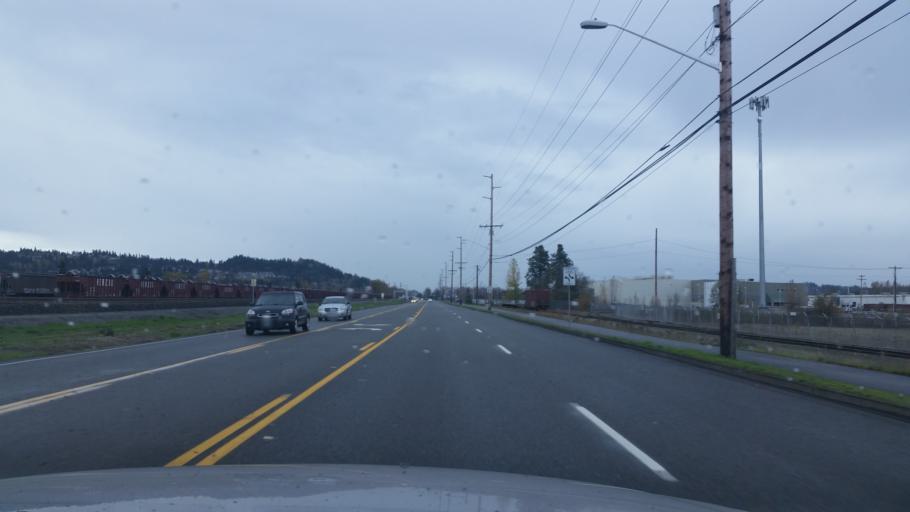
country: US
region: Washington
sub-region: King County
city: Algona
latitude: 47.2842
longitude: -122.2315
